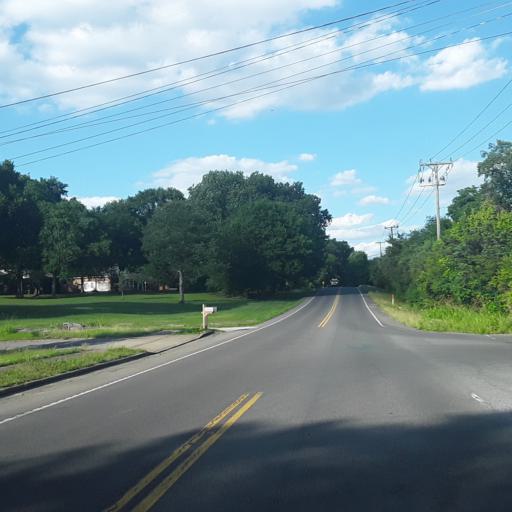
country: US
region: Tennessee
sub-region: Wilson County
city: Green Hill
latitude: 36.1726
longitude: -86.5855
